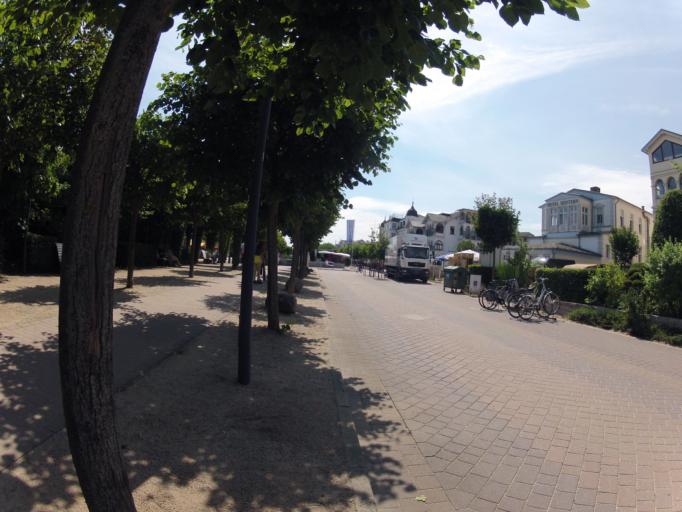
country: DE
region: Mecklenburg-Vorpommern
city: Seebad Heringsdorf
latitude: 53.9435
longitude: 14.1876
